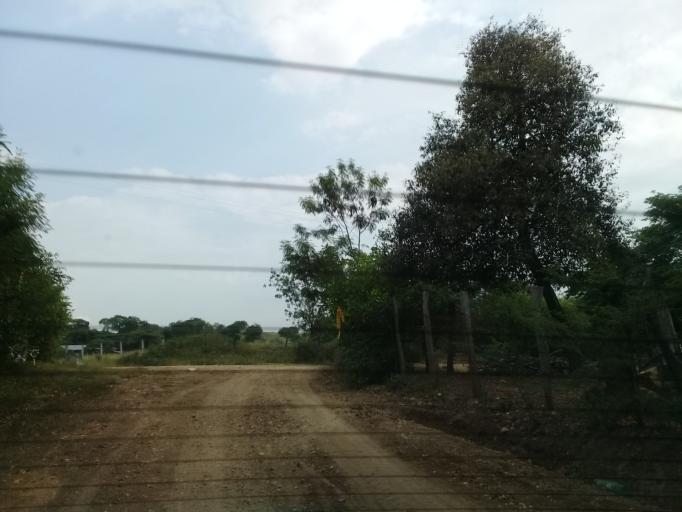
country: CO
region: Cundinamarca
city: Ricaurte
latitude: 4.3476
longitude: -74.7374
